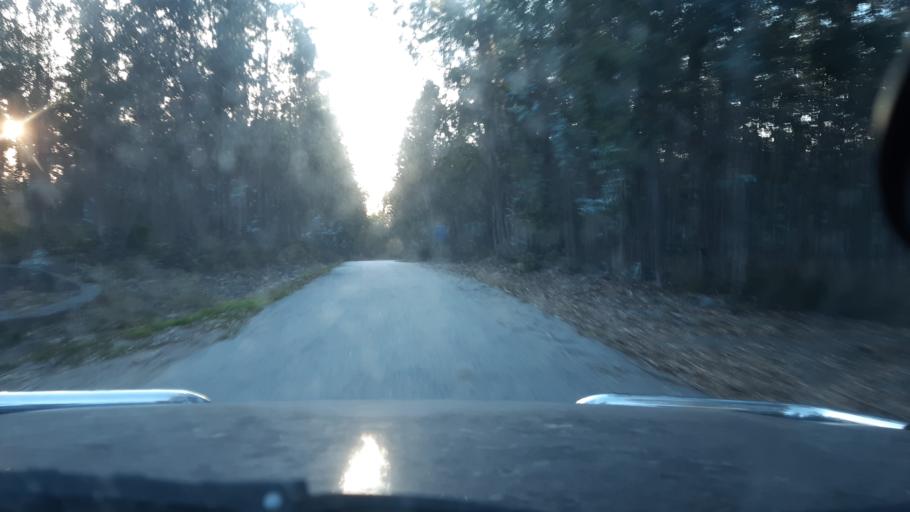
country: PT
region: Aveiro
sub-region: Agueda
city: Aguada de Cima
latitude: 40.5534
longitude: -8.2863
